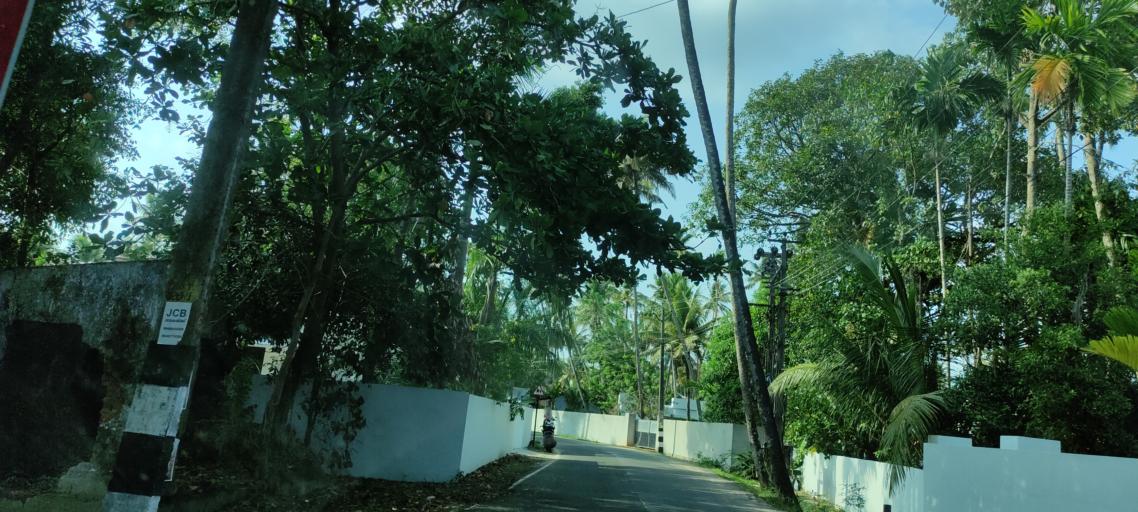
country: IN
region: Kerala
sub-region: Alappuzha
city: Vayalar
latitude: 9.7093
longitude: 76.2886
